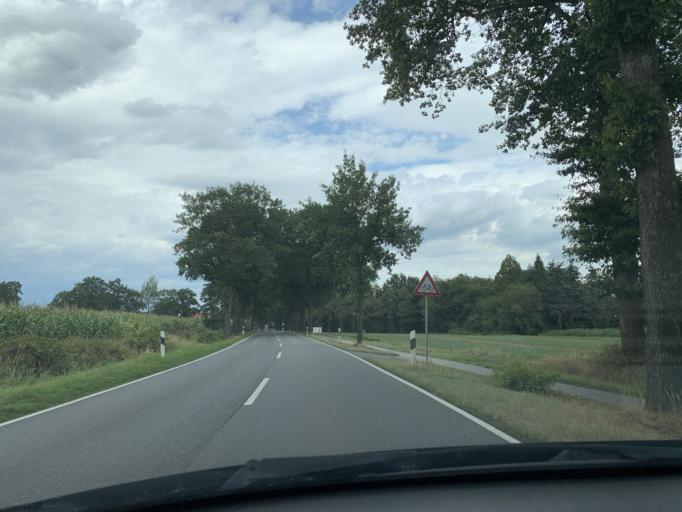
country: DE
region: Lower Saxony
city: Westerstede
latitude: 53.2405
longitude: 7.9188
